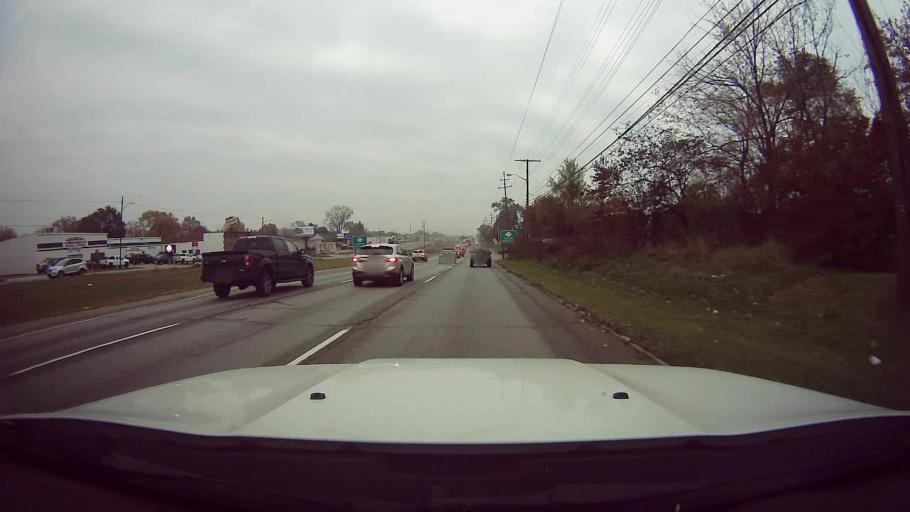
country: US
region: Michigan
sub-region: Wayne County
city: Dearborn Heights
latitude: 42.3334
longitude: -83.2732
